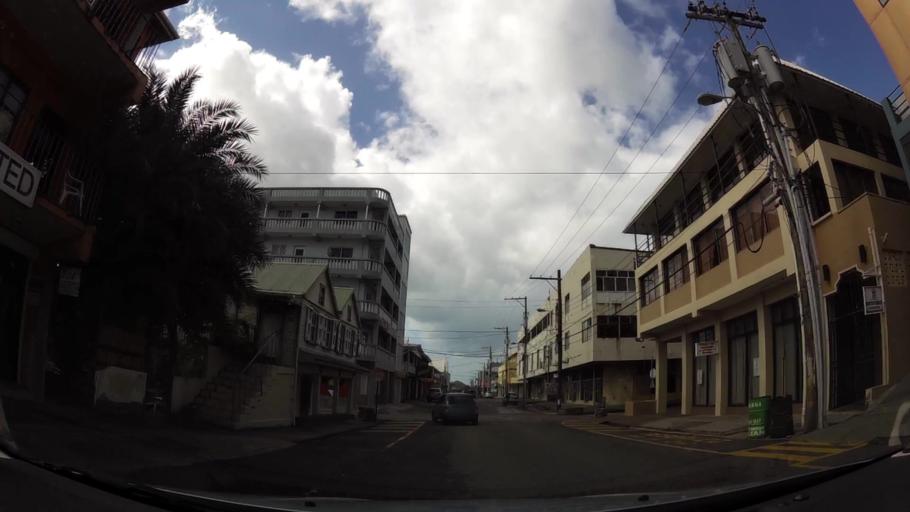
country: AG
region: Saint John
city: Saint John's
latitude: 17.1202
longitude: -61.8431
